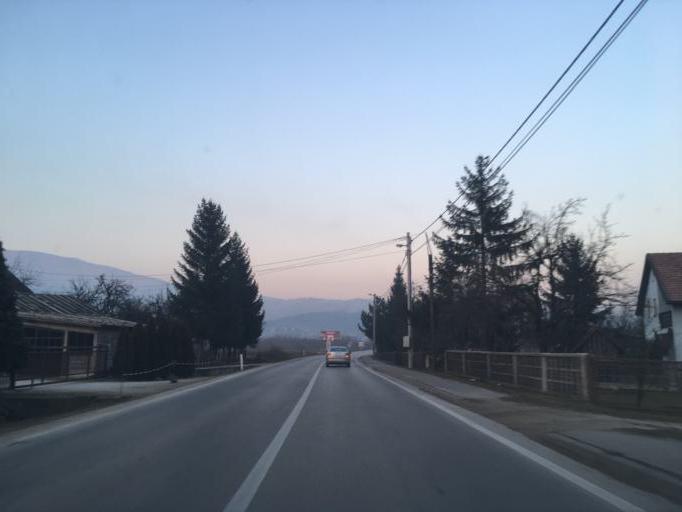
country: BA
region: Federation of Bosnia and Herzegovina
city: Travnik
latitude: 44.2003
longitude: 17.7106
